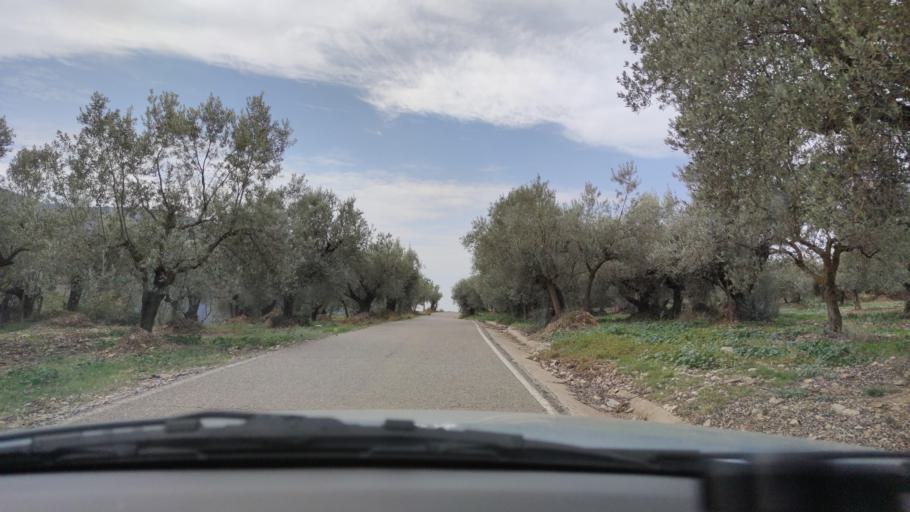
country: ES
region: Catalonia
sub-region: Provincia de Lleida
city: Llimiana
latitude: 42.0698
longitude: 0.9392
